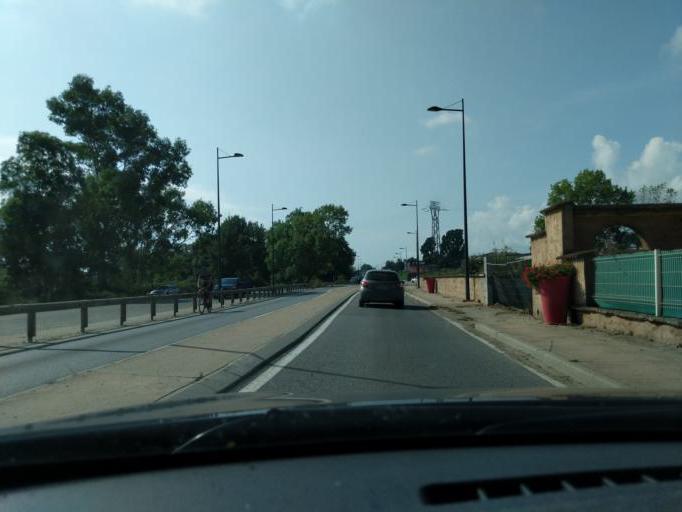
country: FR
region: Corsica
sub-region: Departement de la Haute-Corse
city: Ghisonaccia
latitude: 42.0039
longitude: 9.4031
